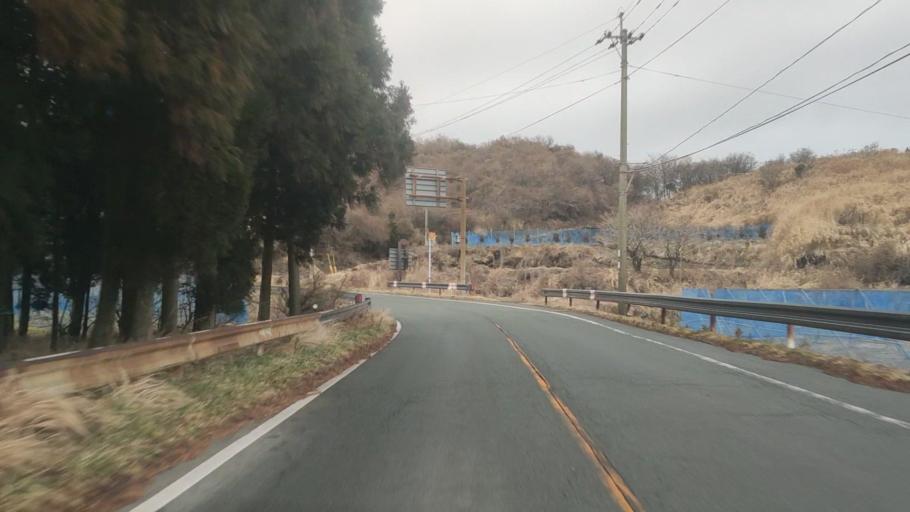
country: JP
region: Kumamoto
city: Aso
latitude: 32.9073
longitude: 131.1590
